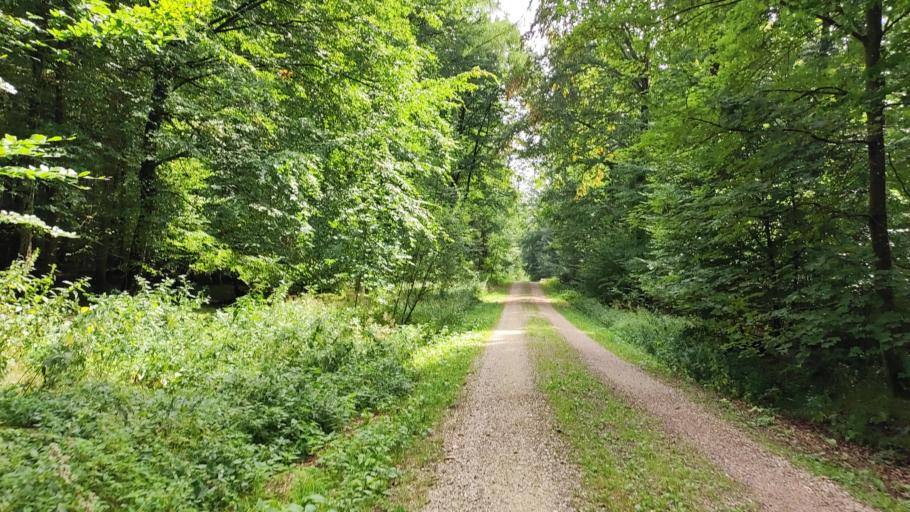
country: DE
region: Bavaria
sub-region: Swabia
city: Landensberg
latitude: 48.4274
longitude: 10.5161
